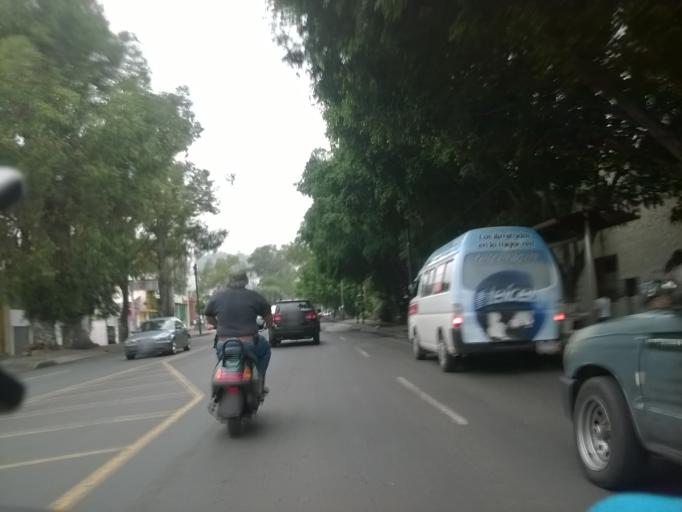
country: MX
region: Michoacan
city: Morelia
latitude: 19.6899
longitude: -101.1799
